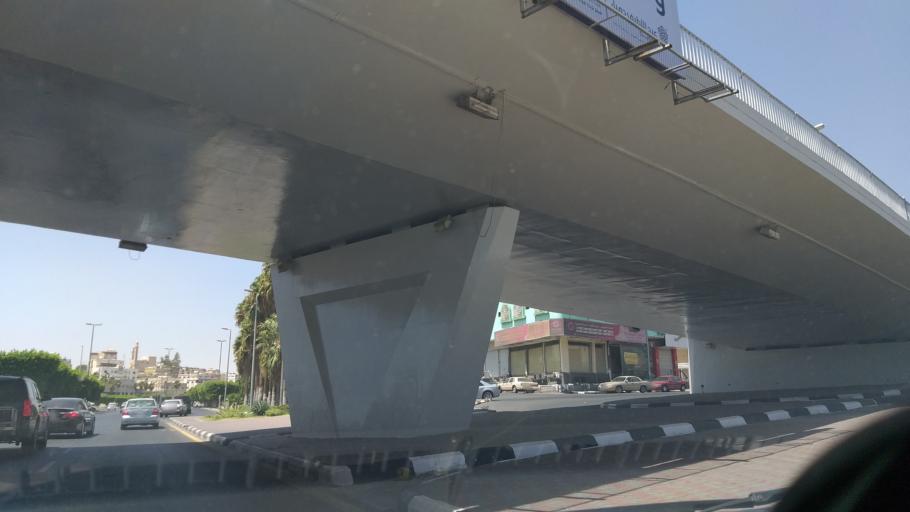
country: SA
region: Makkah
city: Ta'if
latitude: 21.2751
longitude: 40.4217
